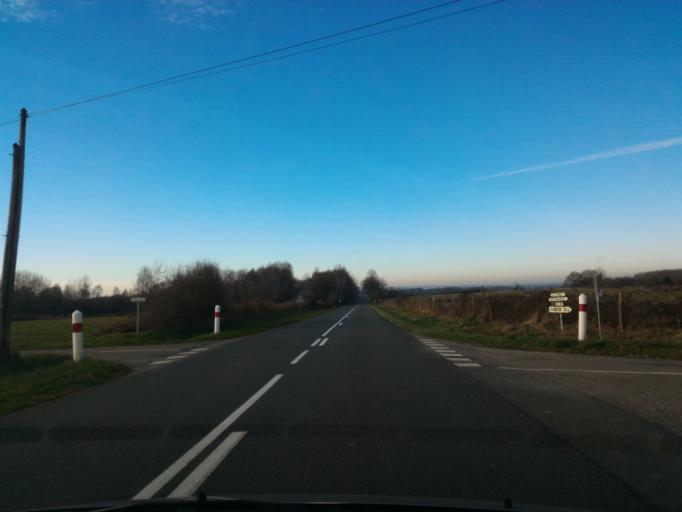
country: FR
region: Poitou-Charentes
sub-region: Departement de la Charente
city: Confolens
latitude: 46.0332
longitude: 0.5828
